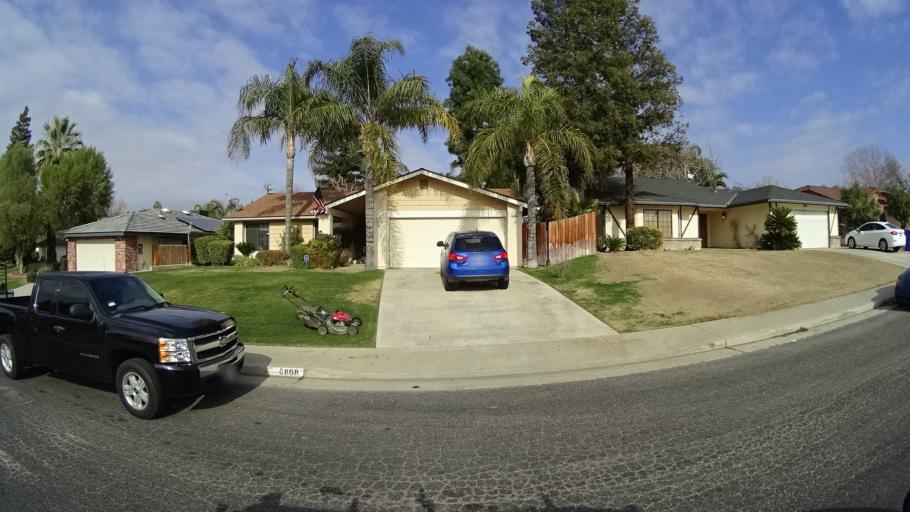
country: US
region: California
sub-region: Kern County
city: Bakersfield
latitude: 35.3886
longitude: -118.9271
